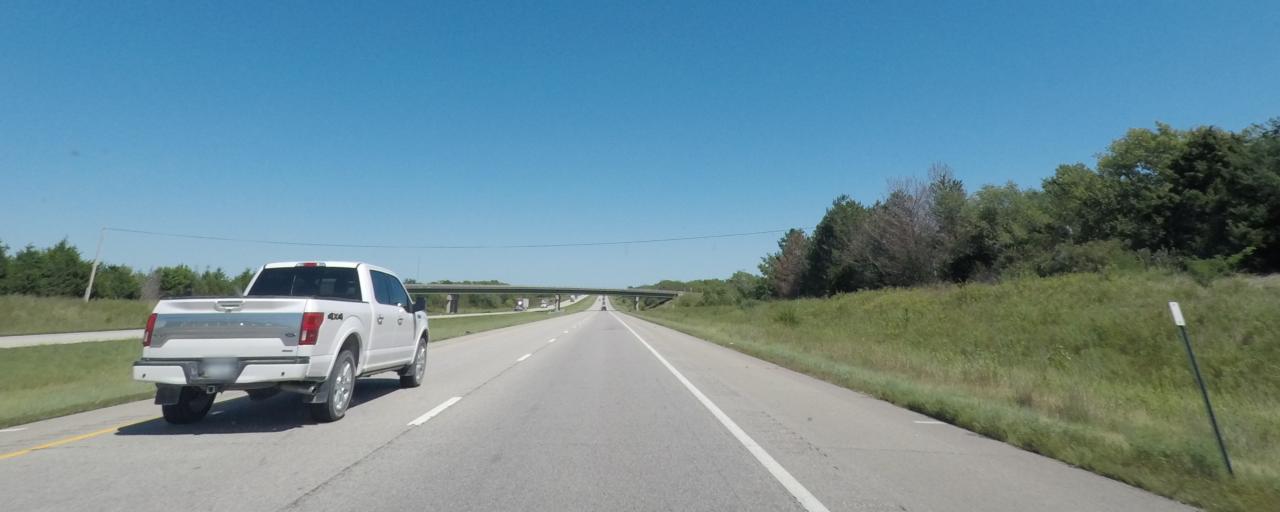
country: US
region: Kansas
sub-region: Lyon County
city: Emporia
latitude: 38.4094
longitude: -95.9695
